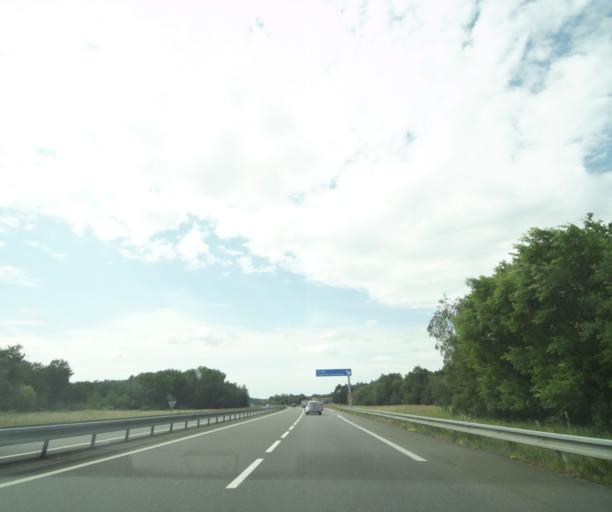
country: FR
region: Pays de la Loire
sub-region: Departement de Maine-et-Loire
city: Jumelles
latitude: 47.4161
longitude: -0.1281
